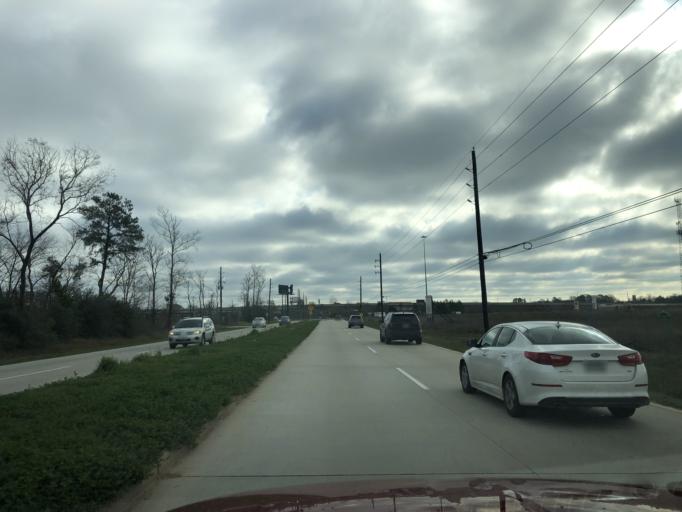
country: US
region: Texas
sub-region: Harris County
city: Spring
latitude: 30.0830
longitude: -95.4414
